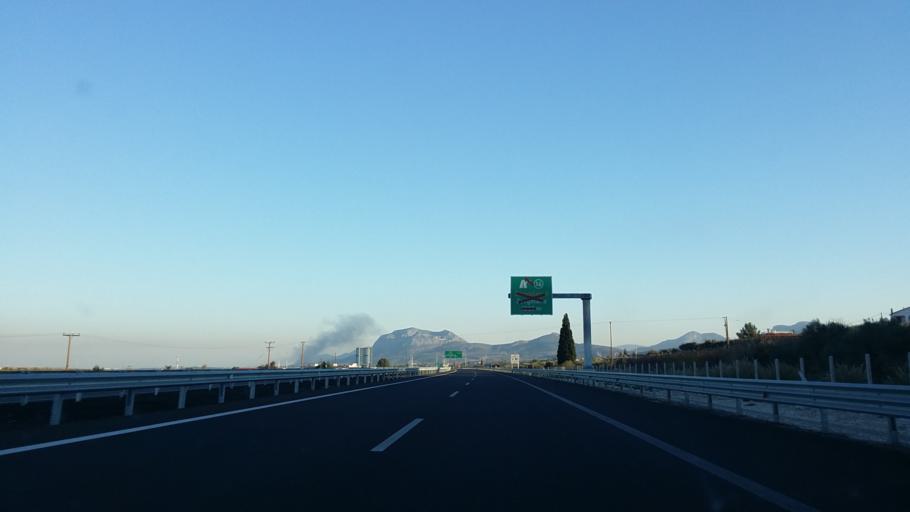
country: GR
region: Peloponnese
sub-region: Nomos Korinthias
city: Vokhaiko
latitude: 37.9350
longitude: 22.7761
